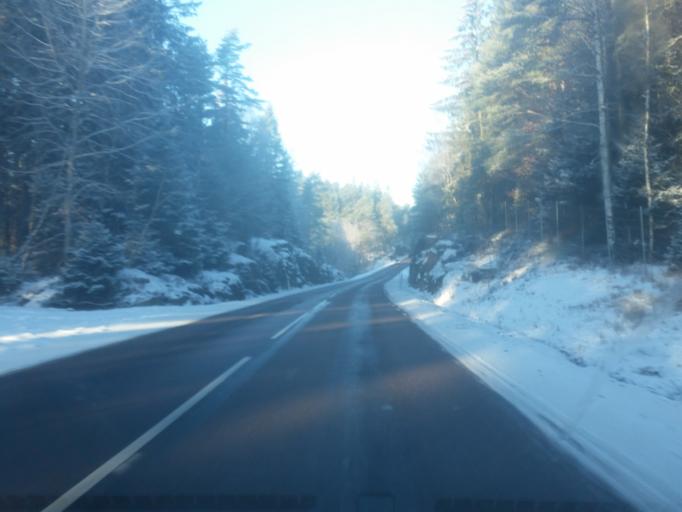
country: SE
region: Vaestra Goetaland
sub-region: Partille Kommun
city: Furulund
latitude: 57.6920
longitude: 12.1611
